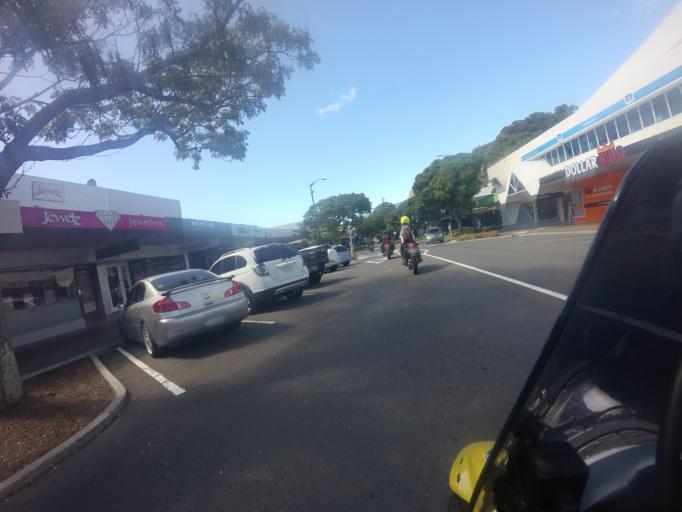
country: NZ
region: Bay of Plenty
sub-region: Whakatane District
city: Whakatane
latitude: -37.9520
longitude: 176.9941
